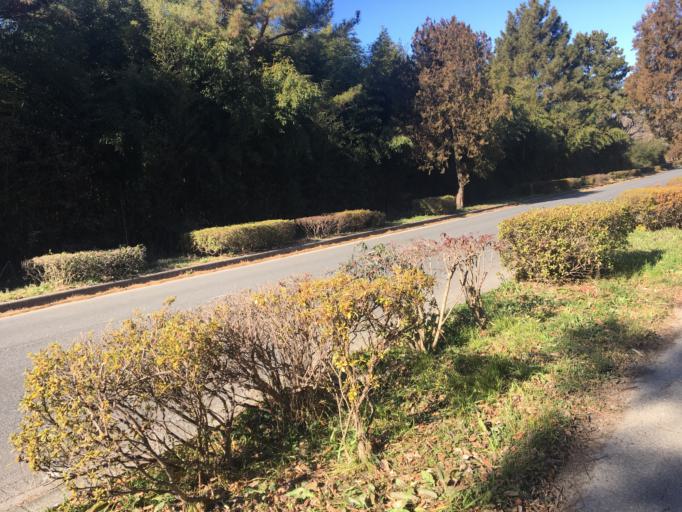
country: JP
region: Saitama
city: Shiki
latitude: 35.8407
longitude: 139.6094
